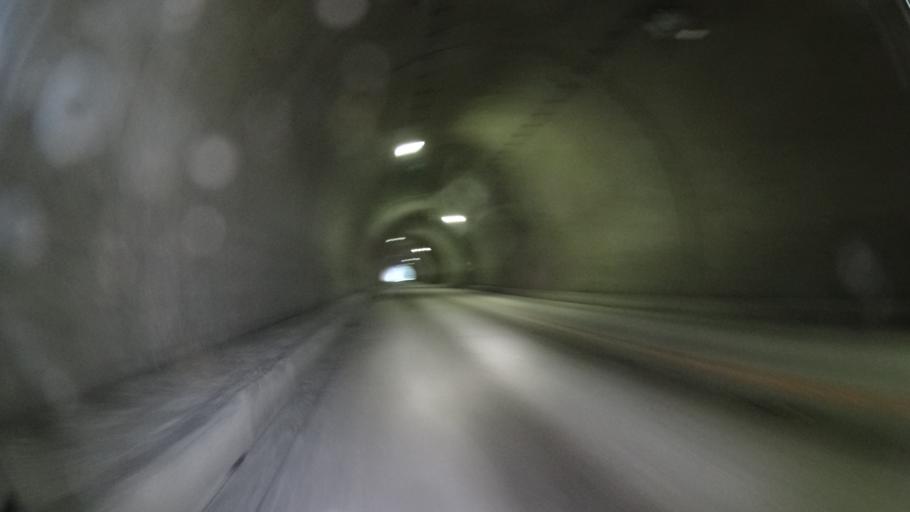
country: JP
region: Yamanashi
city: Enzan
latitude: 35.8063
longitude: 138.8565
